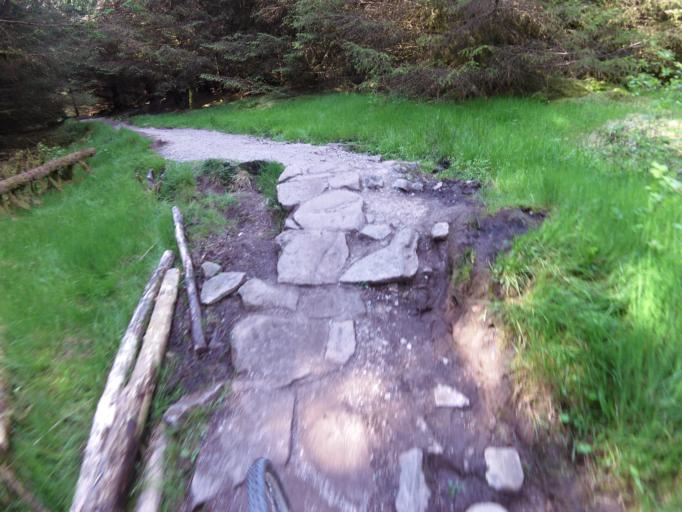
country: GB
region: England
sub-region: North Yorkshire
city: Settle
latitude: 54.0099
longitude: -2.3960
